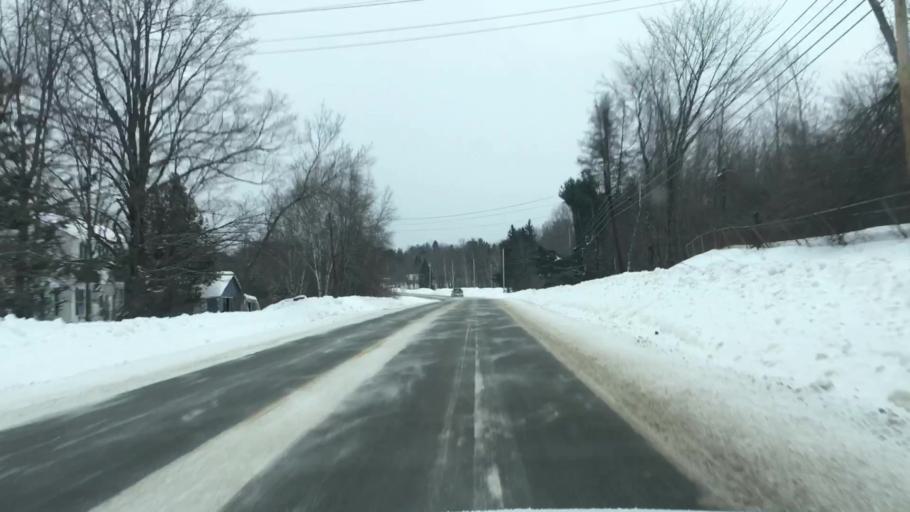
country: US
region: Maine
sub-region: Penobscot County
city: Lincoln
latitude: 45.4031
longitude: -68.4891
